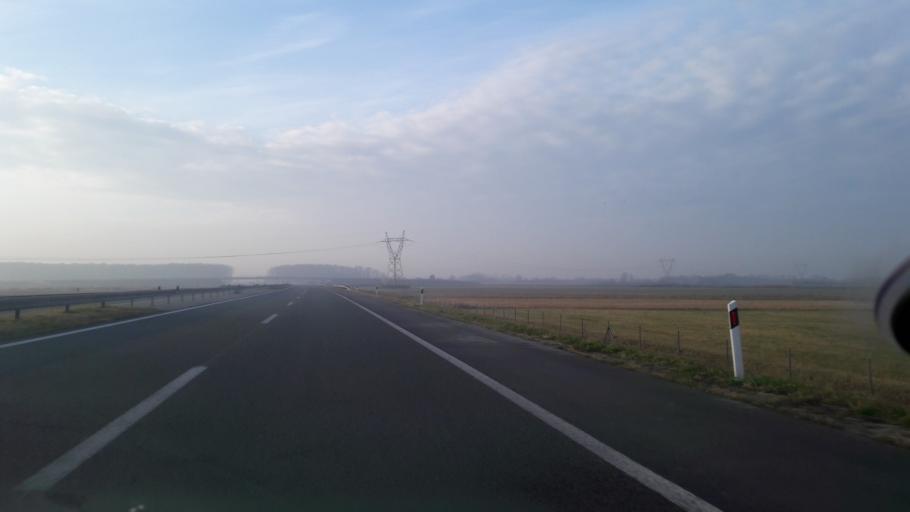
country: HR
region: Osjecko-Baranjska
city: Vuka
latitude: 45.4515
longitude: 18.4653
